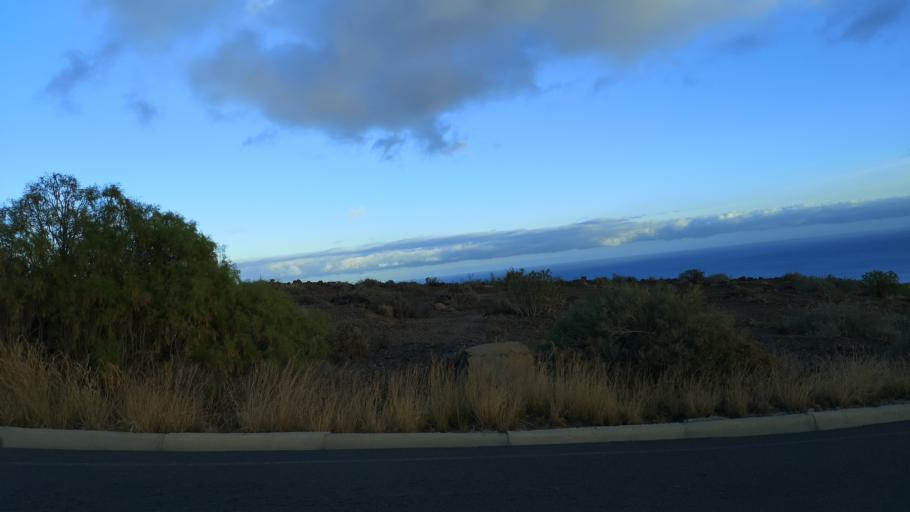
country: ES
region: Canary Islands
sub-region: Provincia de Santa Cruz de Tenerife
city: Alajero
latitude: 28.0346
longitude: -17.2215
